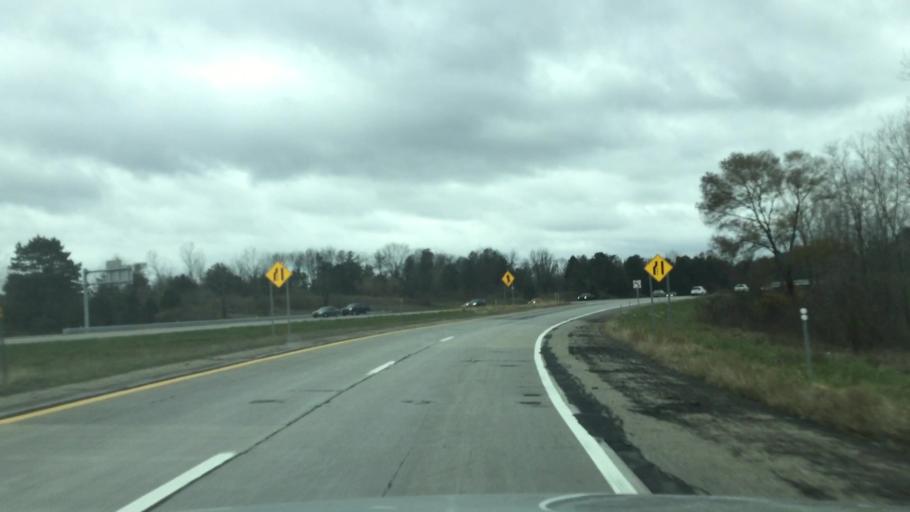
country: US
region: Michigan
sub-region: Washtenaw County
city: Ypsilanti
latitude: 42.3264
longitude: -83.6397
